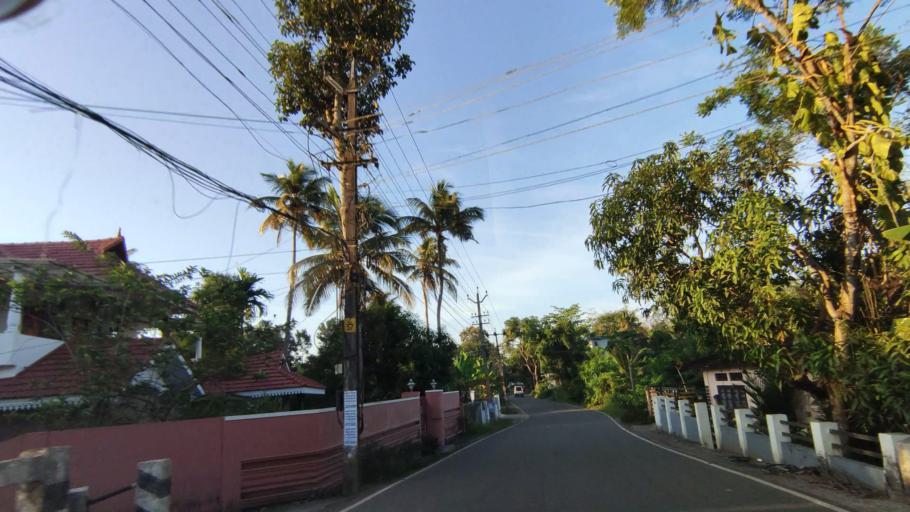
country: IN
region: Kerala
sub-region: Kottayam
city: Kottayam
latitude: 9.6192
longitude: 76.4938
